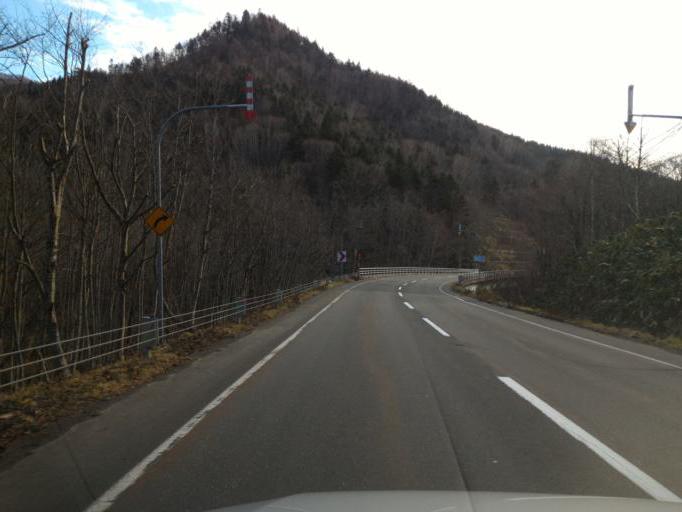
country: JP
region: Hokkaido
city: Shimo-furano
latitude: 43.3626
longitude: 142.2404
